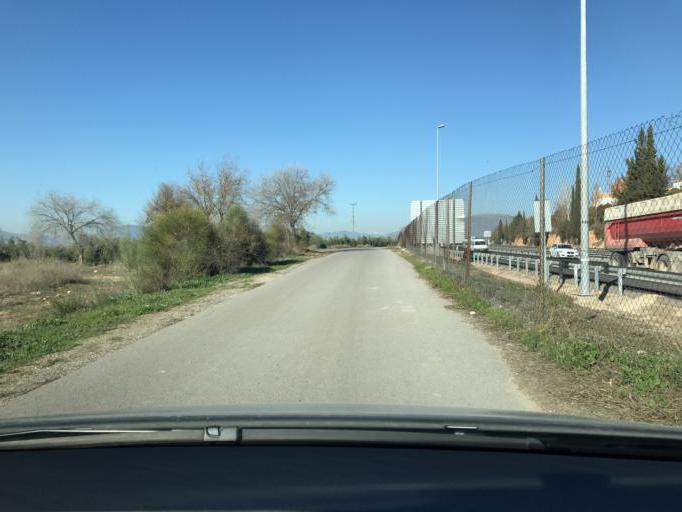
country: ES
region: Andalusia
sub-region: Provincia de Granada
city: Albolote
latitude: 37.2522
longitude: -3.6580
